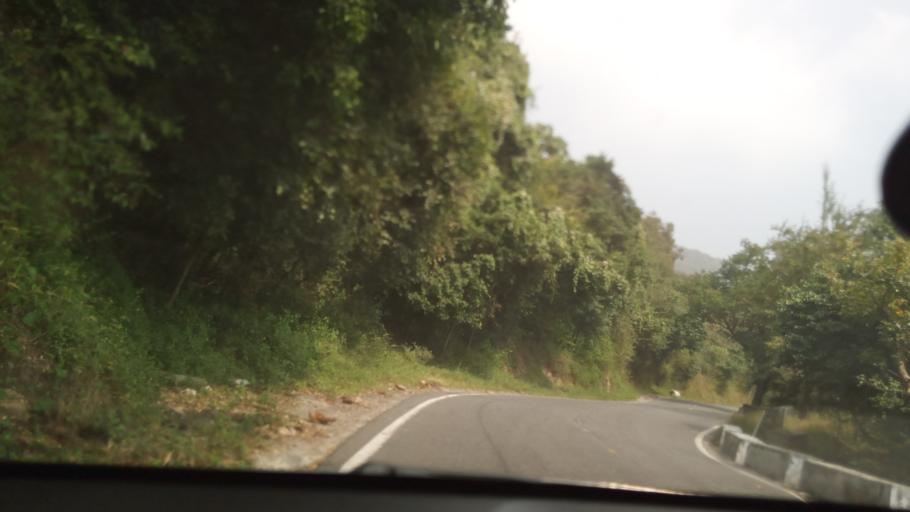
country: IN
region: Tamil Nadu
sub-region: Erode
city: Sathyamangalam
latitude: 11.5989
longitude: 77.1251
